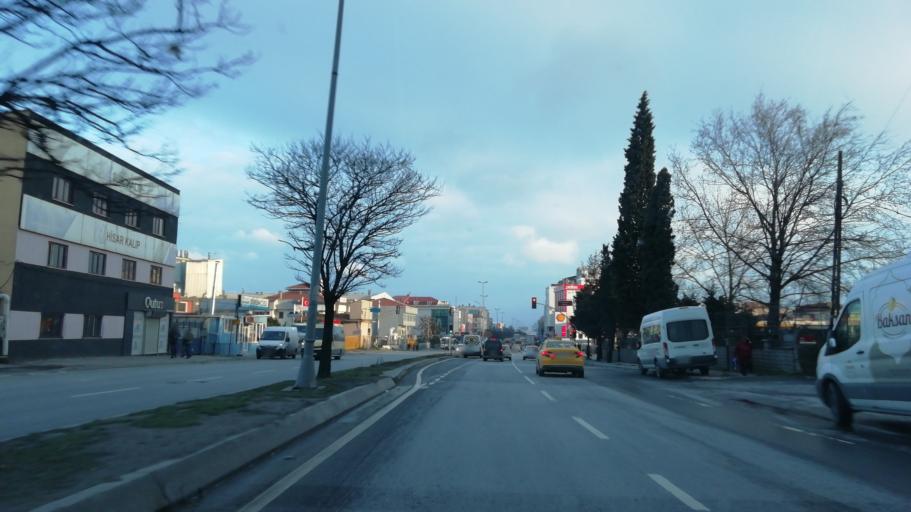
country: TR
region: Istanbul
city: Esenyurt
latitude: 41.0104
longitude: 28.7006
